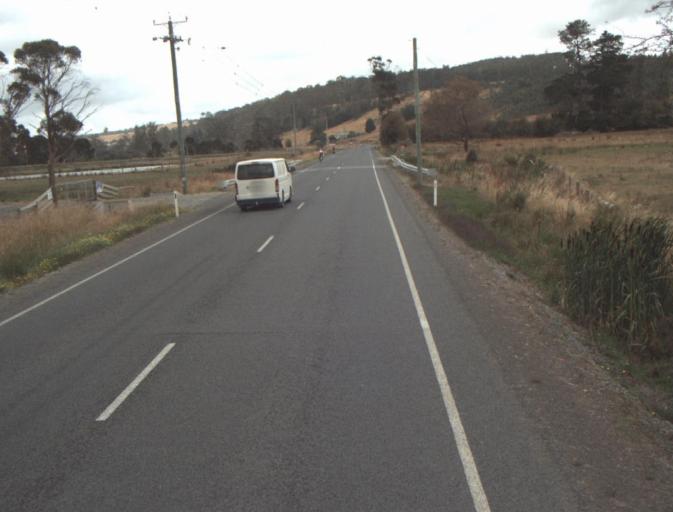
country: AU
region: Tasmania
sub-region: Launceston
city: Mayfield
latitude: -41.2427
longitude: 147.2166
